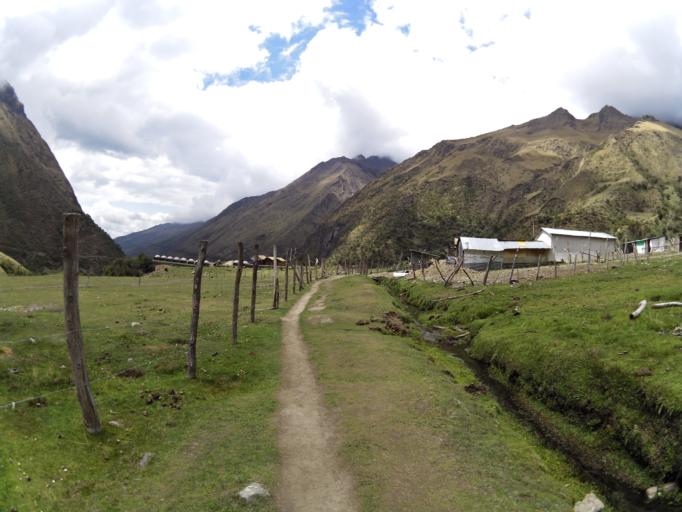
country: PE
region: Cusco
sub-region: Provincia de Anta
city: Limatambo
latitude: -13.3892
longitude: -72.5740
